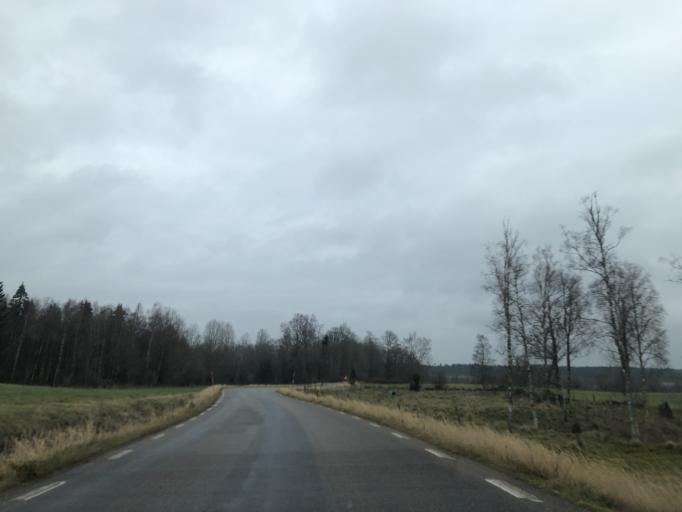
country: SE
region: Vaestra Goetaland
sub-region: Ulricehamns Kommun
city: Ulricehamn
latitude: 57.8909
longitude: 13.5102
